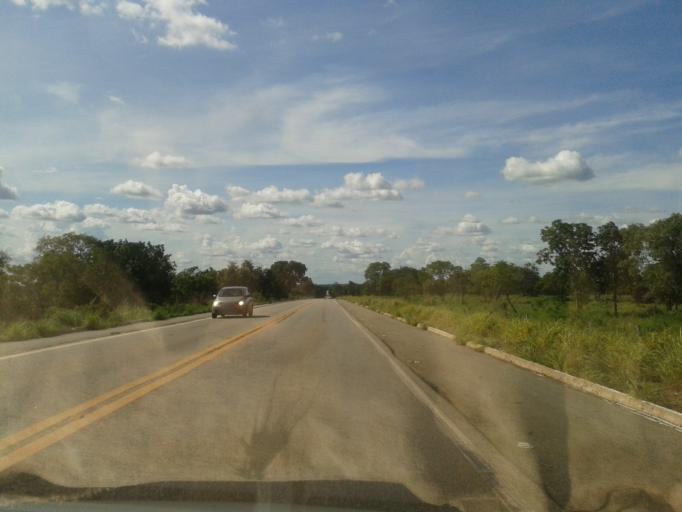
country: BR
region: Goias
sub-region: Mozarlandia
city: Mozarlandia
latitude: -15.2451
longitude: -50.5078
